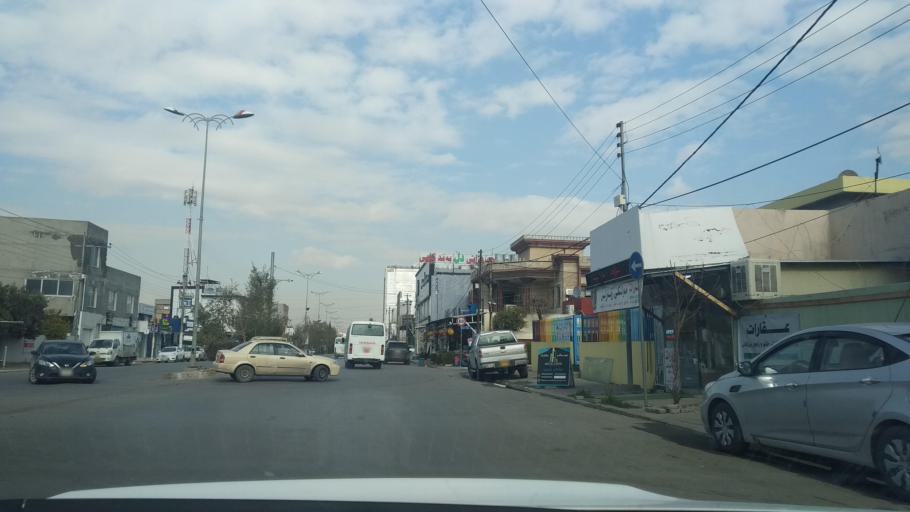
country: IQ
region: Arbil
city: Erbil
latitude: 36.1789
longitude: 44.0366
